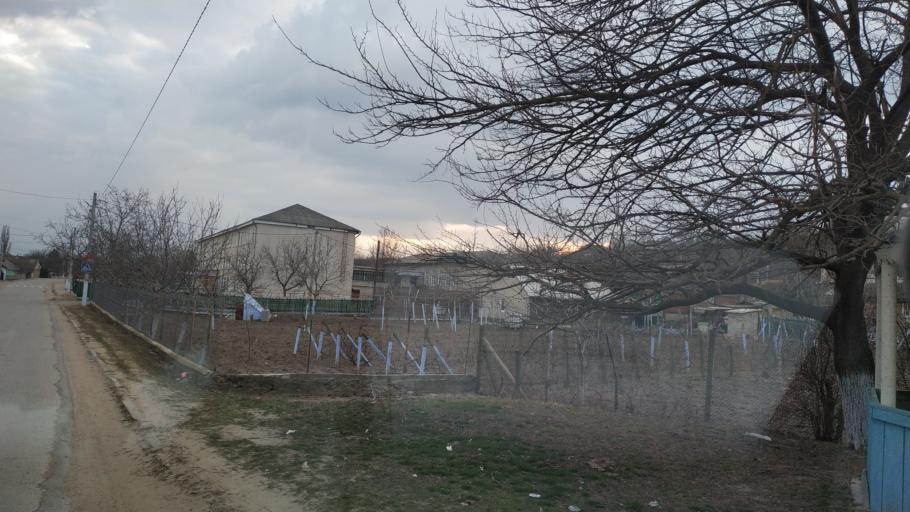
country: MD
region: Telenesti
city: Grigoriopol
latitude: 47.0212
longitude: 29.3575
